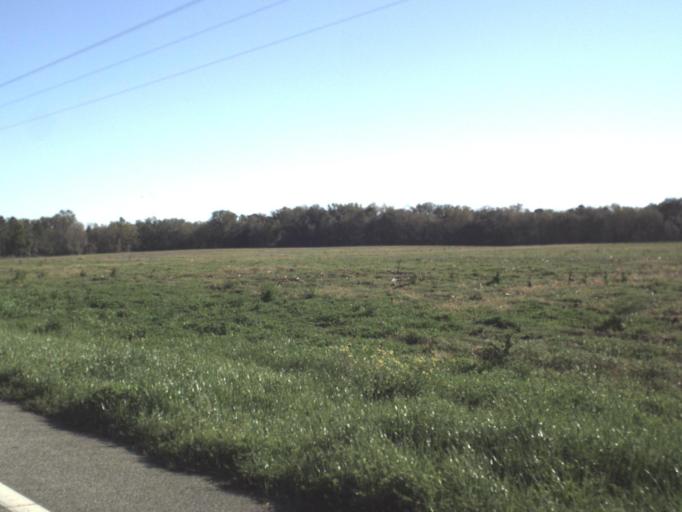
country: US
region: Georgia
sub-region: Brooks County
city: Quitman
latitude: 30.6359
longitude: -83.6449
